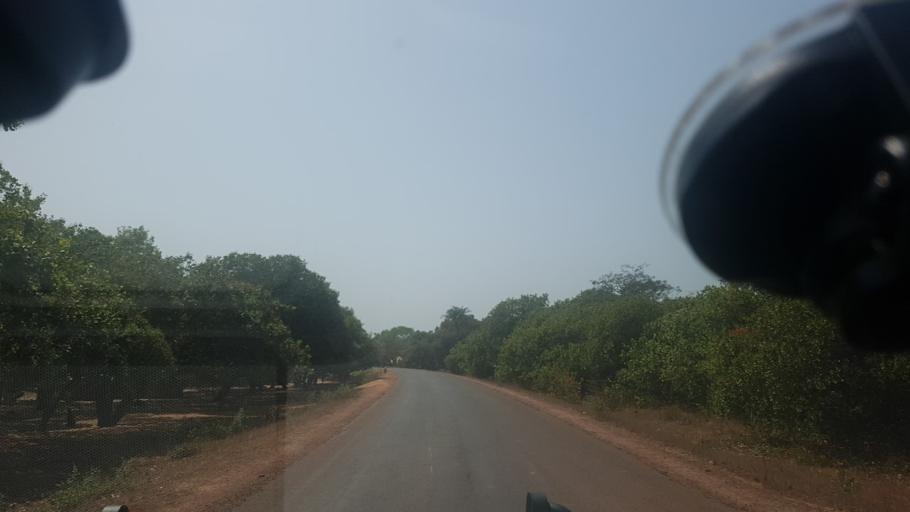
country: GW
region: Cacheu
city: Cacheu
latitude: 12.4127
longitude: -16.0727
